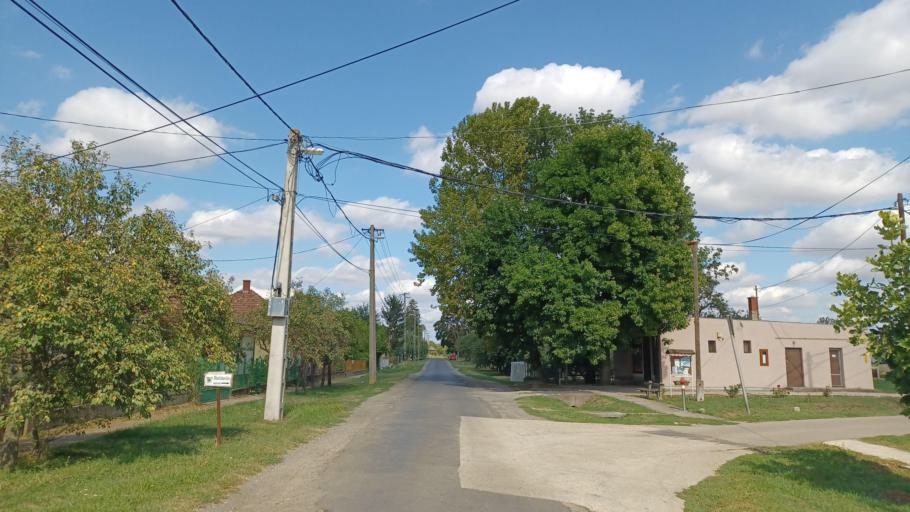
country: HU
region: Tolna
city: Pincehely
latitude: 46.7234
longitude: 18.4748
